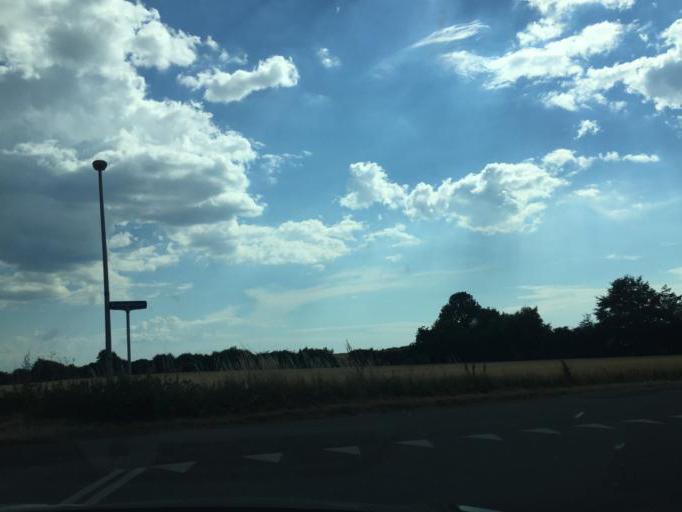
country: DK
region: South Denmark
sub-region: Assens Kommune
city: Assens
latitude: 55.2080
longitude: 10.0010
